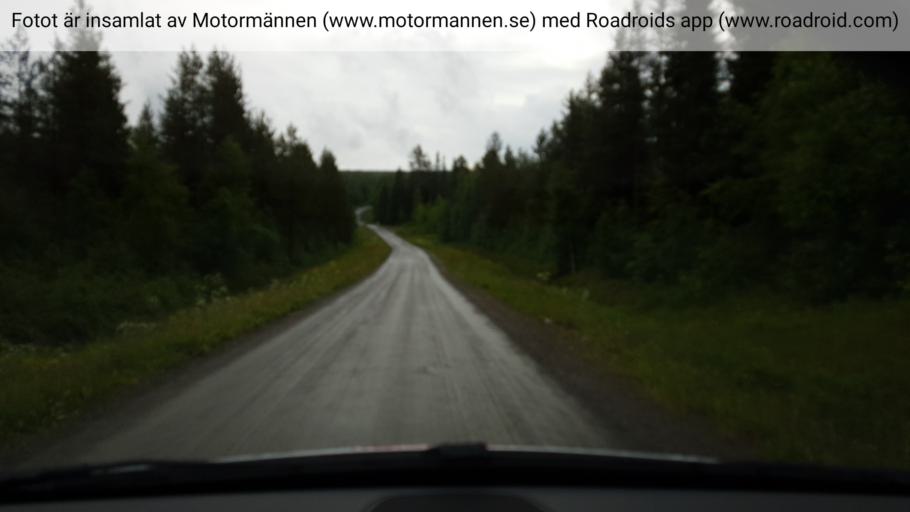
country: SE
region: Jaemtland
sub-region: Stroemsunds Kommun
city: Stroemsund
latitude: 64.2707
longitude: 15.0102
